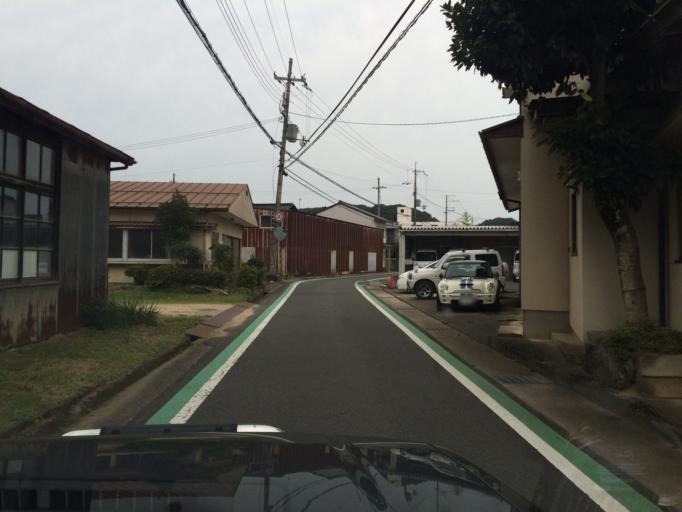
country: JP
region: Hyogo
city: Toyooka
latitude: 35.4636
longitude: 134.7718
